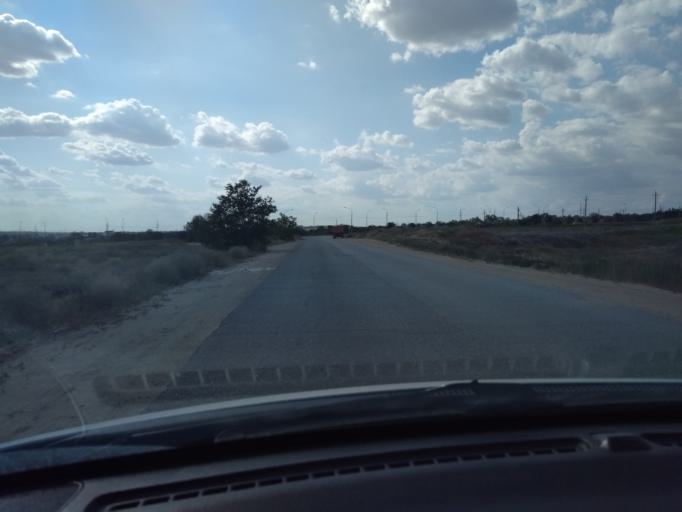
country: RU
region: Volgograd
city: Vodstroy
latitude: 48.8064
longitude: 44.5260
